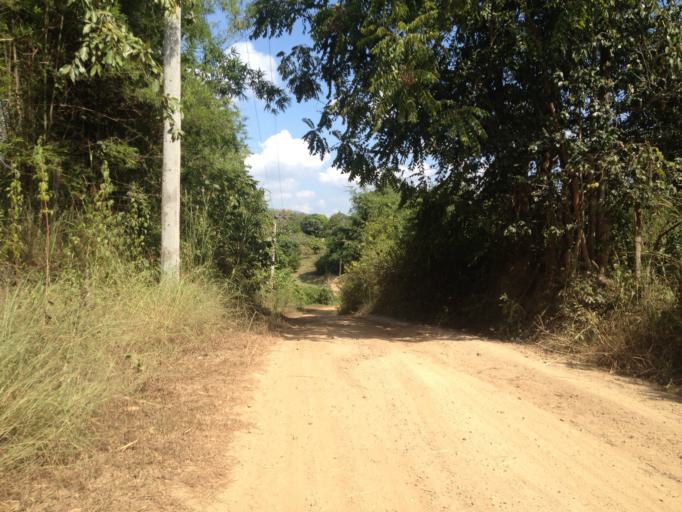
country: TH
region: Chiang Mai
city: Hang Dong
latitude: 18.7121
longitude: 98.8731
